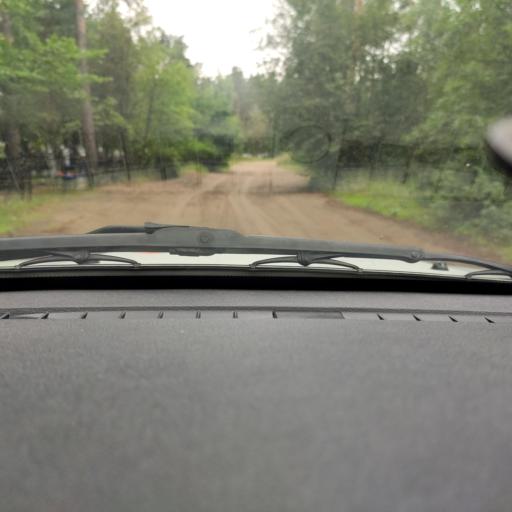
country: RU
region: Voronezj
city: Maslovka
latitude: 51.5766
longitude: 39.2929
